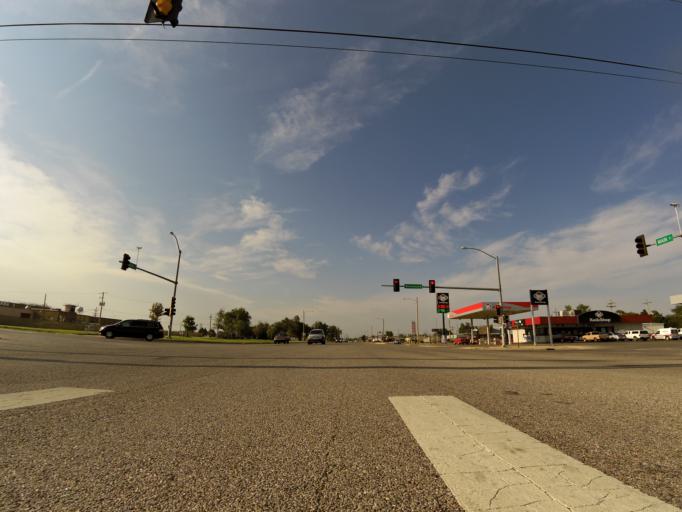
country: US
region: Kansas
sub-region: Reno County
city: South Hutchinson
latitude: 38.0278
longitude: -97.9402
